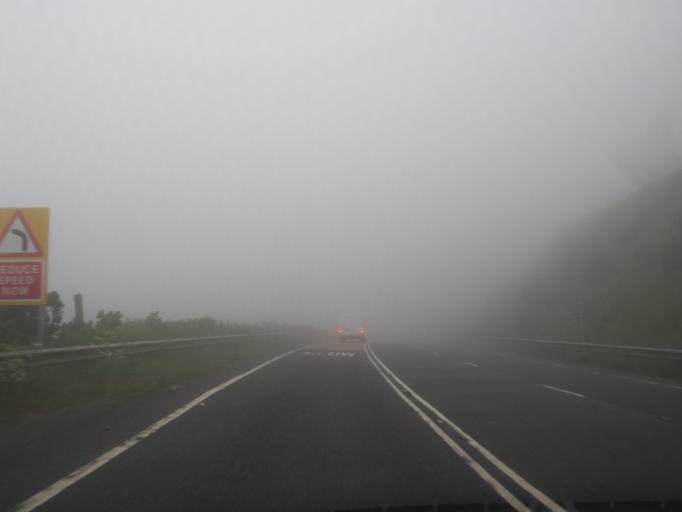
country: GB
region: Scotland
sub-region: Highland
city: Brora
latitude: 58.1411
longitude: -3.6084
